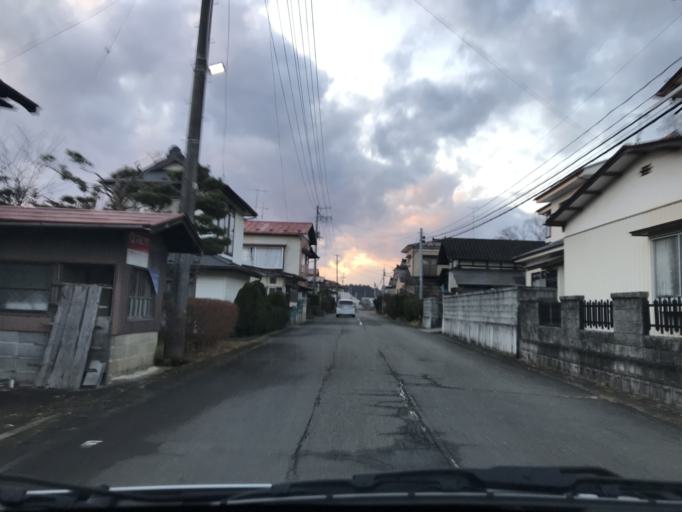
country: JP
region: Iwate
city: Ichinoseki
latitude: 38.8026
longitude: 141.1179
